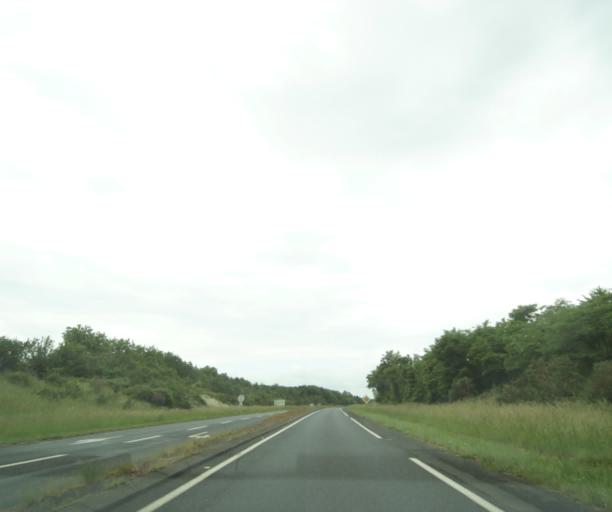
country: FR
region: Poitou-Charentes
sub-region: Departement des Deux-Sevres
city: Saint-Varent
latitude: 46.8594
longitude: -0.2090
